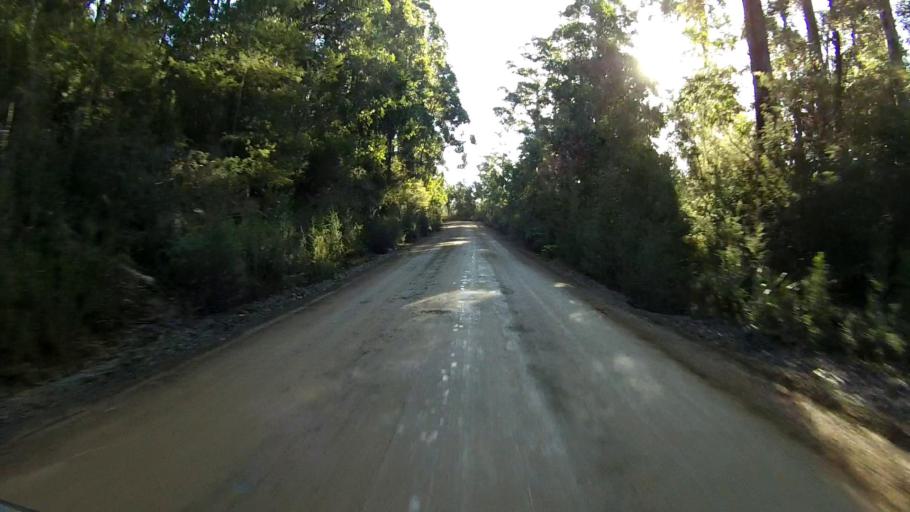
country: AU
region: Tasmania
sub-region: Clarence
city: Sandford
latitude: -43.1204
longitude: 147.9247
